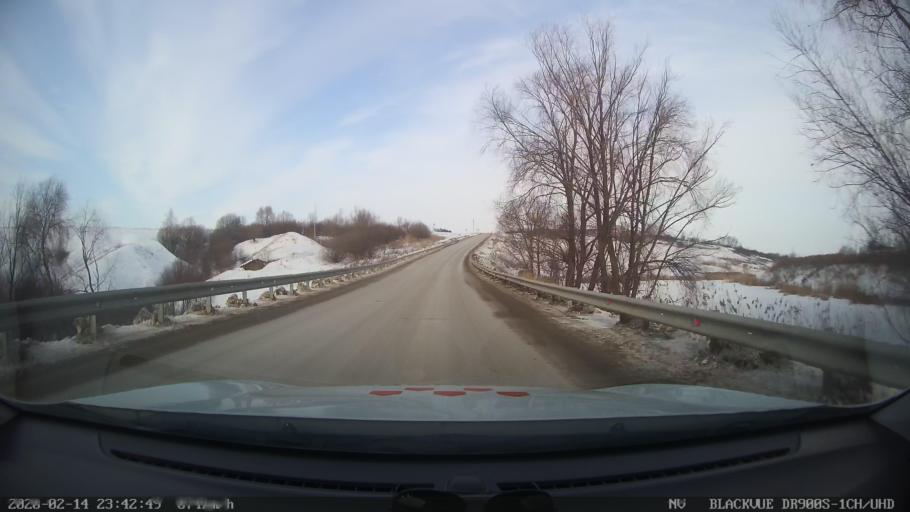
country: RU
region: Tatarstan
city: Kuybyshevskiy Zaton
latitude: 55.1950
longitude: 49.2473
